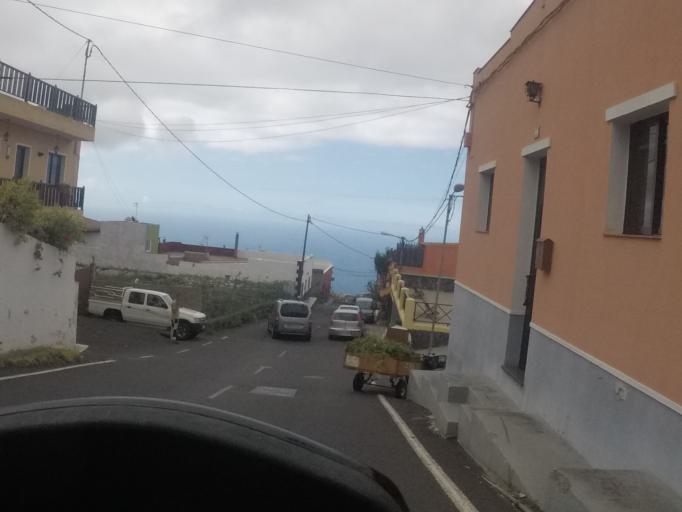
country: ES
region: Canary Islands
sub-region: Provincia de Santa Cruz de Tenerife
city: Icod de los Vinos
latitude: 28.3550
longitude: -16.7069
